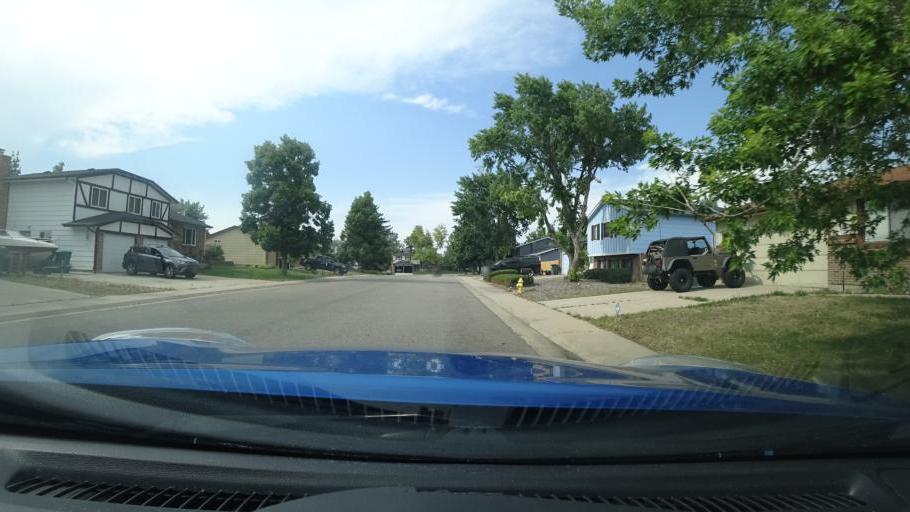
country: US
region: Colorado
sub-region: Adams County
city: Aurora
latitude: 39.6880
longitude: -104.8000
